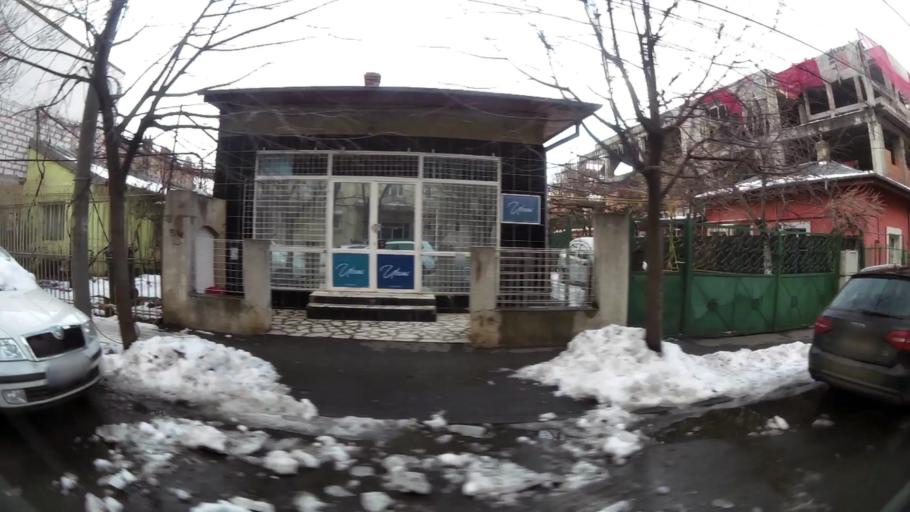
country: RO
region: Bucuresti
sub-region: Municipiul Bucuresti
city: Bucharest
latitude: 44.4200
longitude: 26.1433
